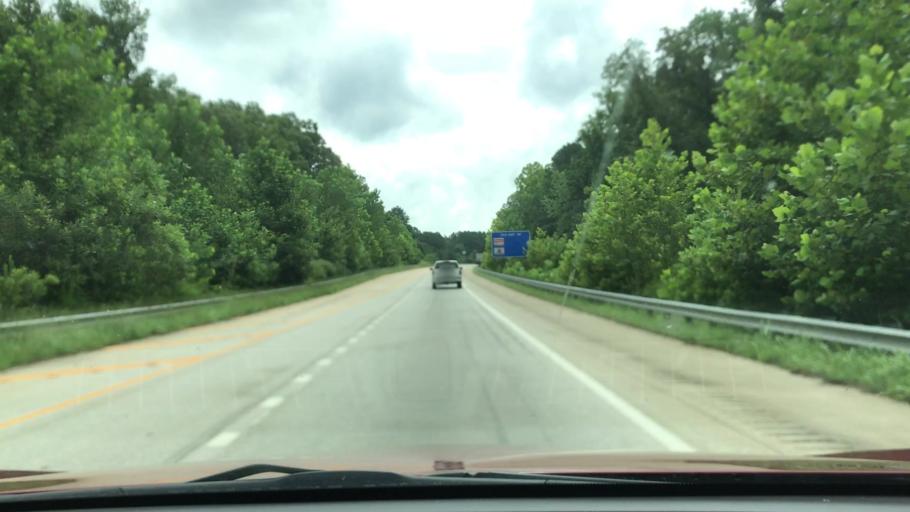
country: US
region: South Carolina
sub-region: Laurens County
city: Clinton
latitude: 34.5131
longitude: -81.8730
